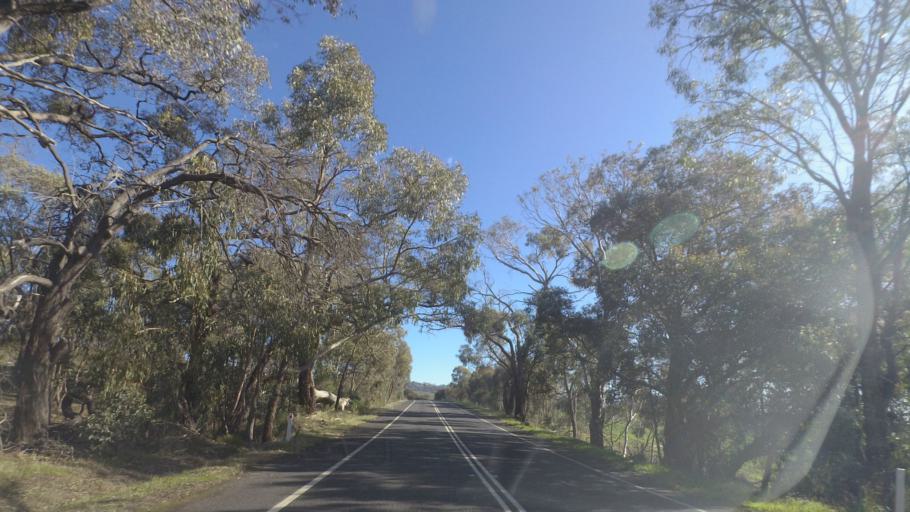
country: AU
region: Victoria
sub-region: Greater Bendigo
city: Kennington
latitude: -36.9106
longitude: 144.3232
